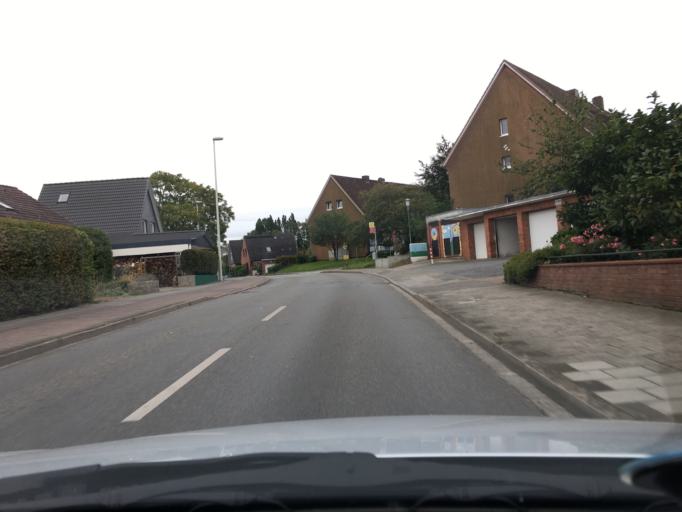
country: DE
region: Schleswig-Holstein
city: Kronshagen
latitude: 54.3386
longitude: 10.0799
